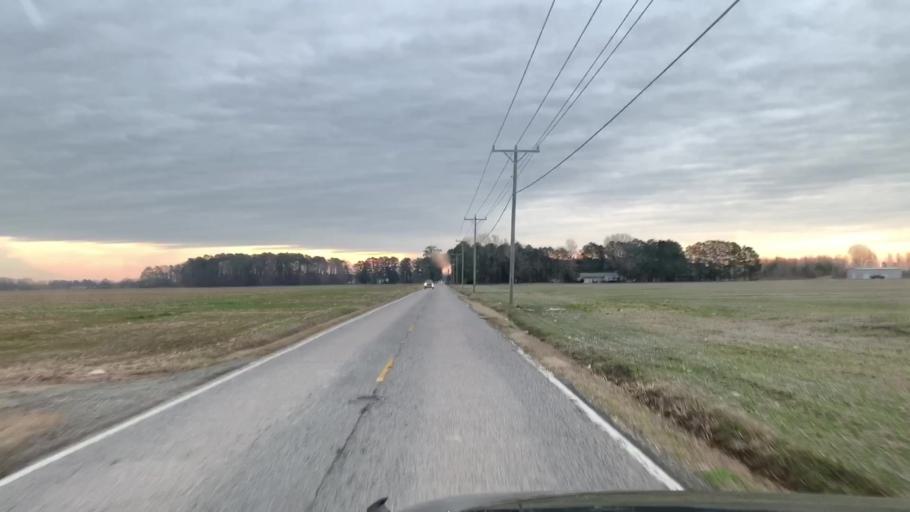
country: US
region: North Carolina
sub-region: Currituck County
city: Moyock
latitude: 36.6335
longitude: -76.1847
